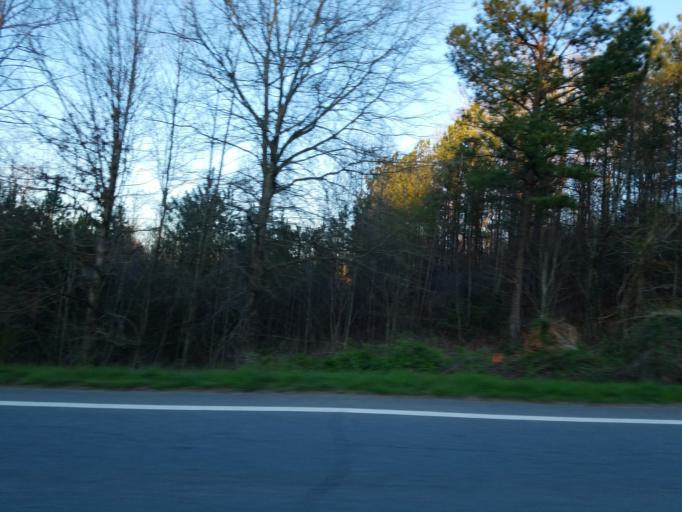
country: US
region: Georgia
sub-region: Dawson County
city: Dawsonville
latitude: 34.3445
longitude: -84.0239
